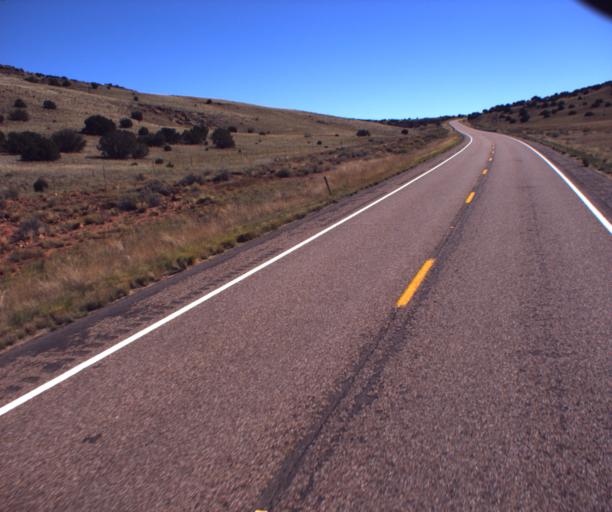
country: US
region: Arizona
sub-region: Apache County
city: Saint Johns
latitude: 34.5712
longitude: -109.5225
